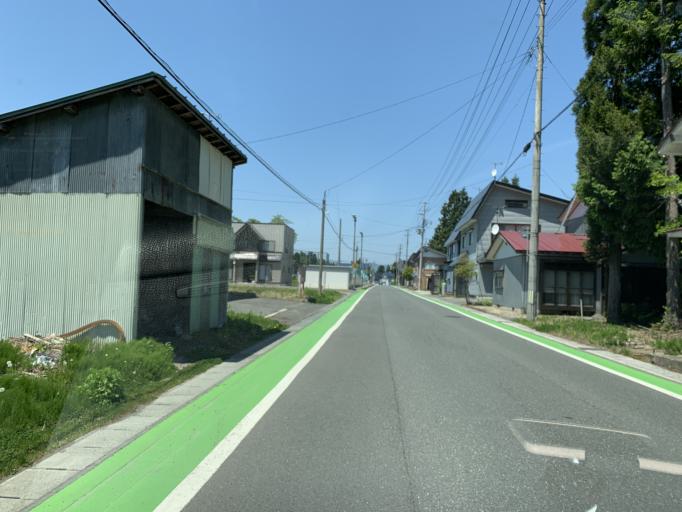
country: JP
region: Akita
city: Yokotemachi
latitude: 39.3497
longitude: 140.7699
